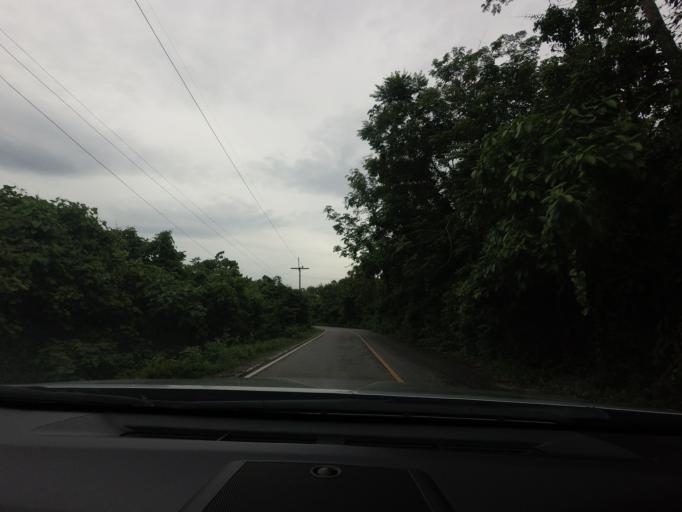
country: TH
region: Narathiwat
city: Rueso
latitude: 6.4145
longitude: 101.5212
